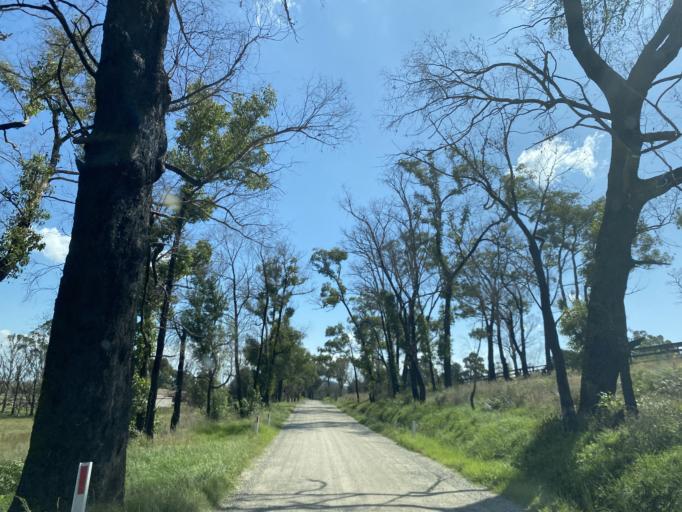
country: AU
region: Victoria
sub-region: Cardinia
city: Bunyip
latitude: -38.0392
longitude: 145.7419
